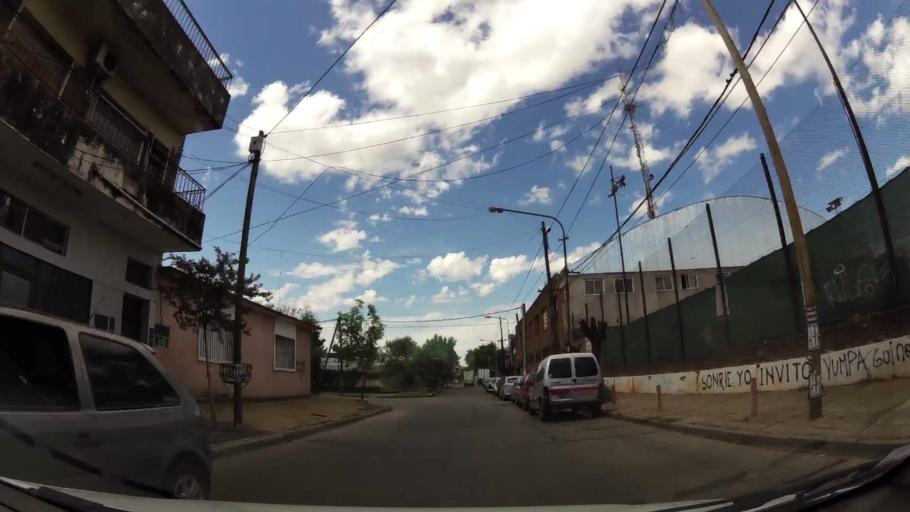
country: AR
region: Buenos Aires
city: San Justo
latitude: -34.6517
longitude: -58.5514
